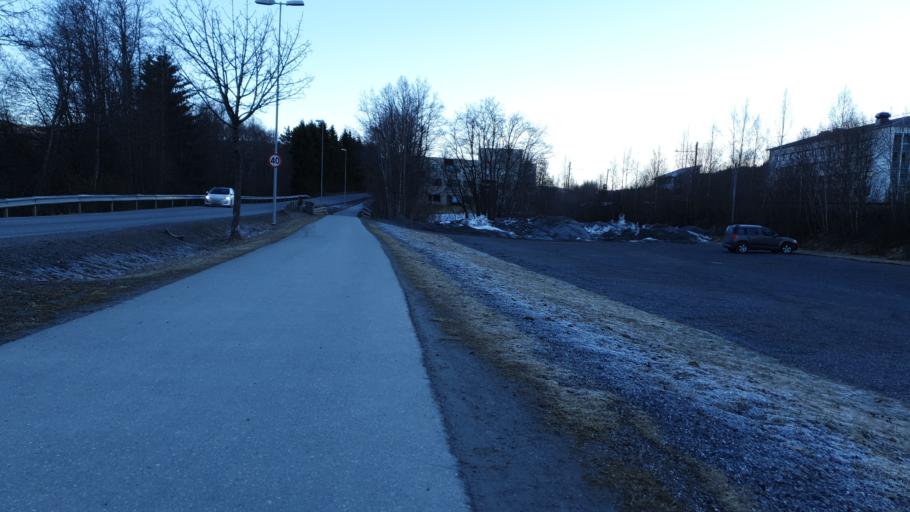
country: NO
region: Sor-Trondelag
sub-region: Orkdal
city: Orkanger
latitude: 63.2907
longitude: 9.8433
